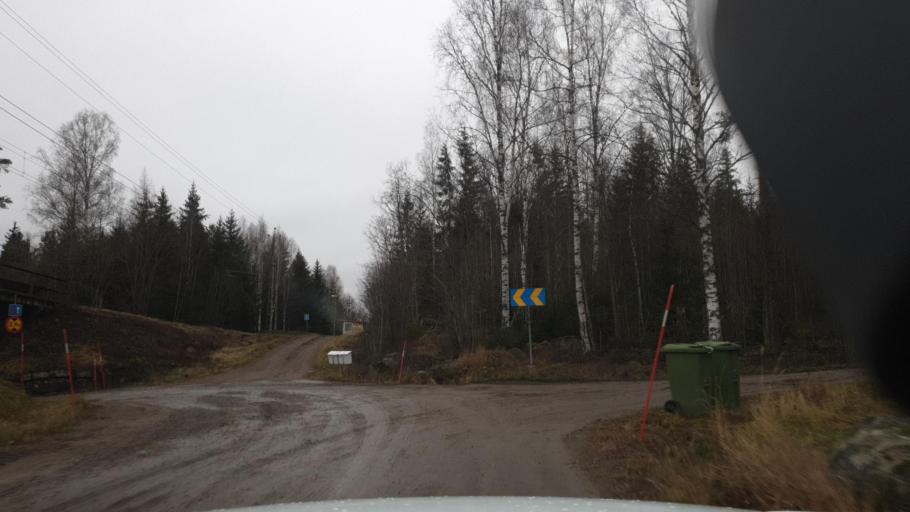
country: SE
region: Vaermland
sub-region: Eda Kommun
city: Amotfors
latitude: 59.8257
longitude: 12.3635
